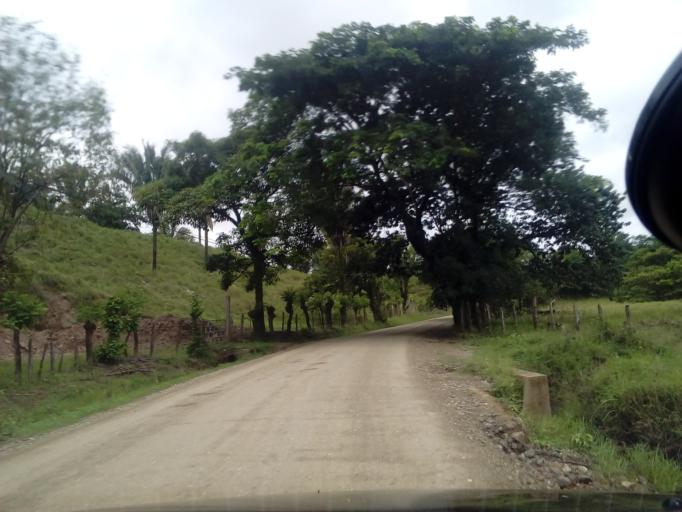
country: CR
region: Guanacaste
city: Samara
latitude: 9.9206
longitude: -85.5634
